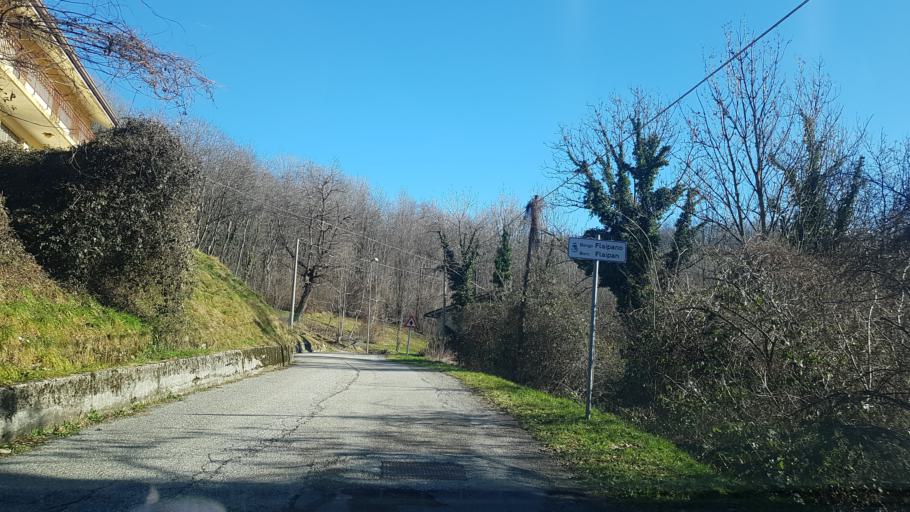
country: IT
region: Friuli Venezia Giulia
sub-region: Provincia di Udine
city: Isola
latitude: 46.2688
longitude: 13.2156
